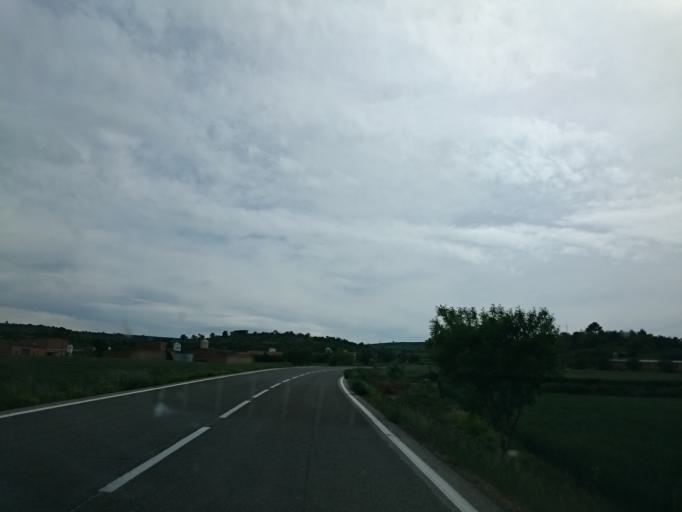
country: ES
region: Catalonia
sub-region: Provincia de Lleida
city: Ivorra
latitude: 41.7758
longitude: 1.3889
